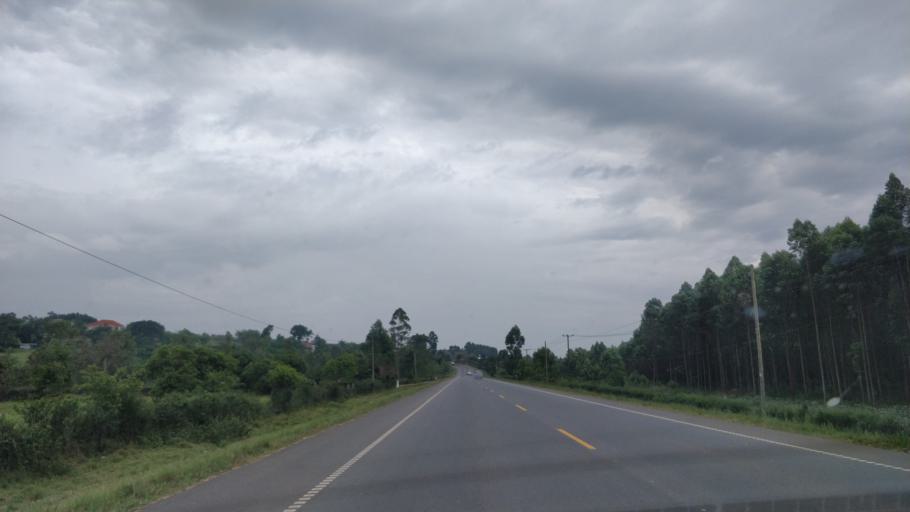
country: UG
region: Western Region
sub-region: Sheema District
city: Kibingo
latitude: -0.6566
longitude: 30.4759
